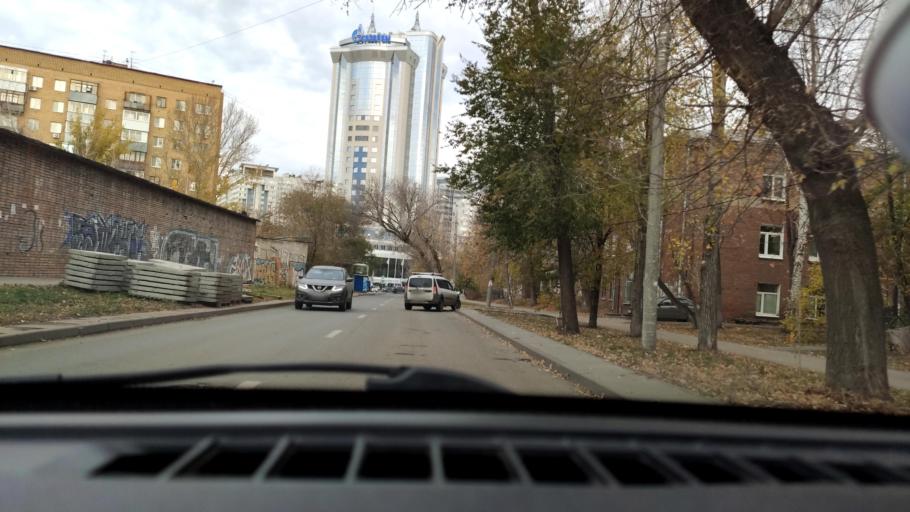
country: RU
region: Samara
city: Samara
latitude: 53.2174
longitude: 50.1549
